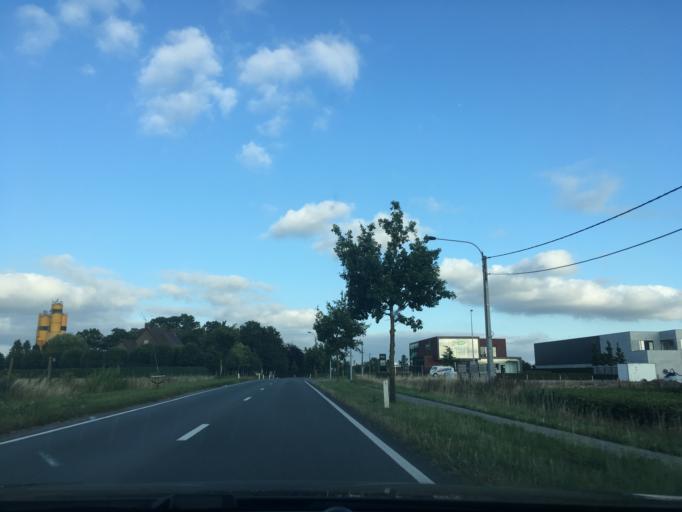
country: BE
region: Flanders
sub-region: Provincie West-Vlaanderen
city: Wingene
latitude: 51.0530
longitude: 3.2886
